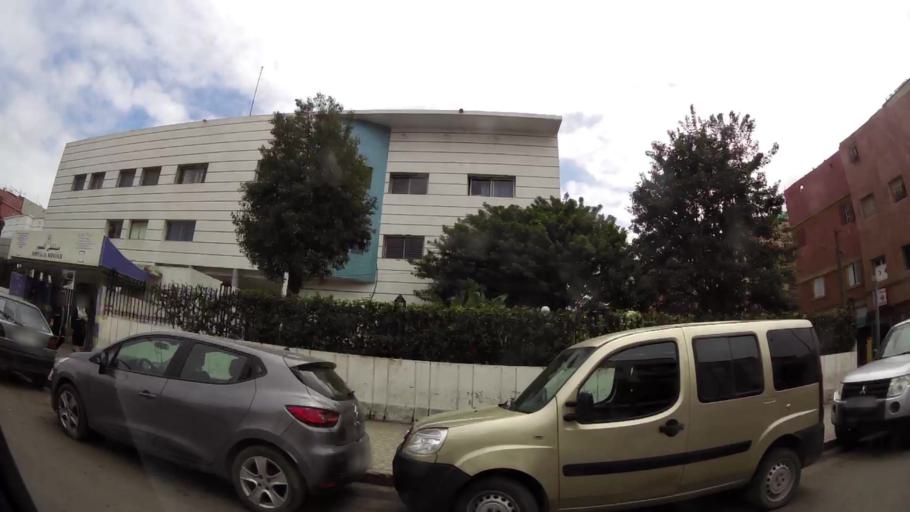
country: MA
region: Grand Casablanca
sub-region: Mediouna
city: Tit Mellil
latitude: 33.6077
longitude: -7.5035
